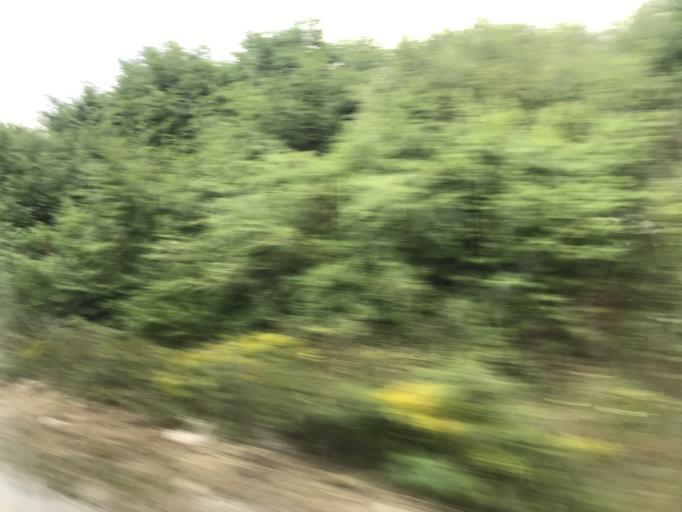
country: GR
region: East Macedonia and Thrace
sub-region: Nomos Rodopis
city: Sapes
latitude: 40.9656
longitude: 25.6445
